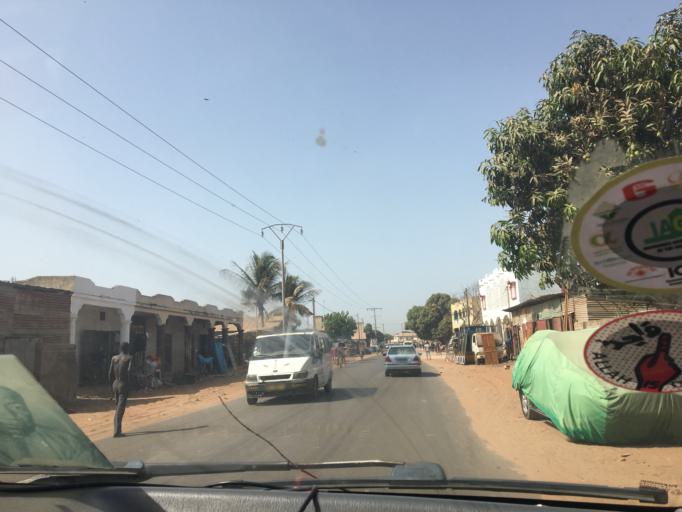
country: GM
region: Western
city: Abuko
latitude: 13.3884
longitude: -16.6762
